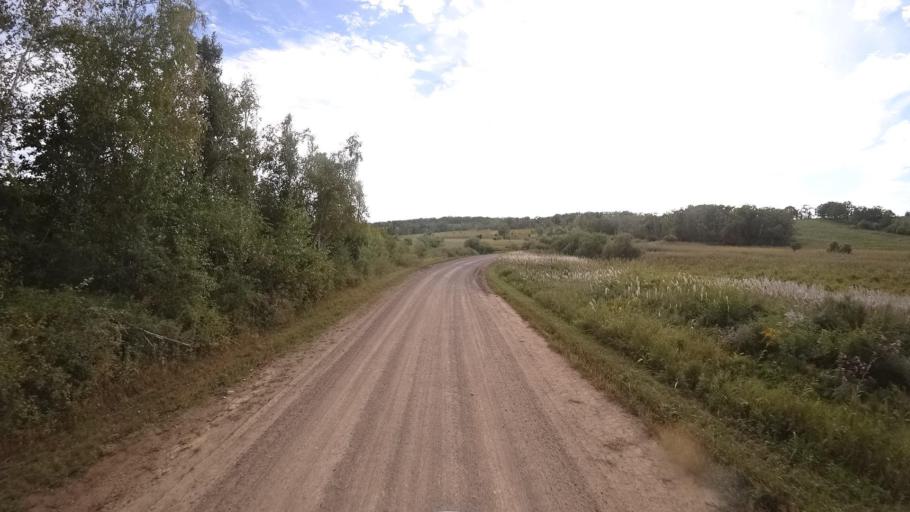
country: RU
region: Primorskiy
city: Dostoyevka
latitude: 44.3689
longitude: 133.5248
